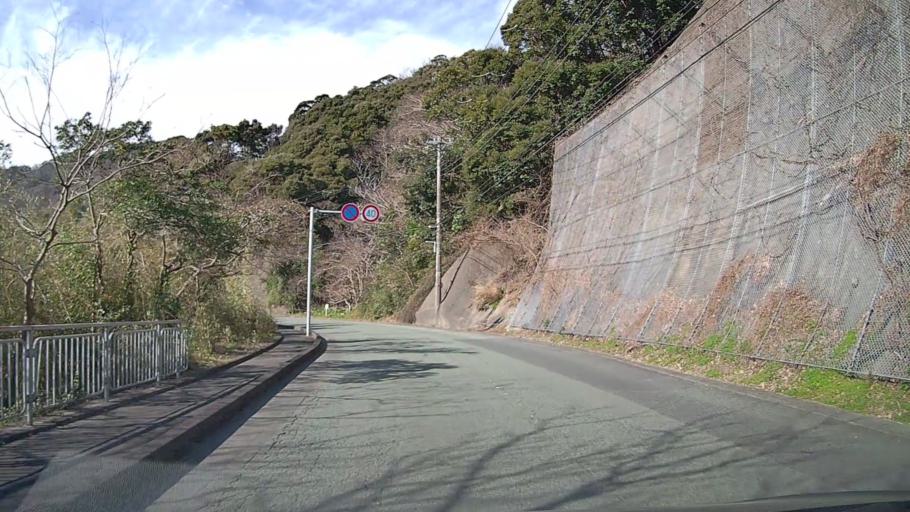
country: JP
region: Shizuoka
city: Shimoda
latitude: 34.6813
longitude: 138.9392
